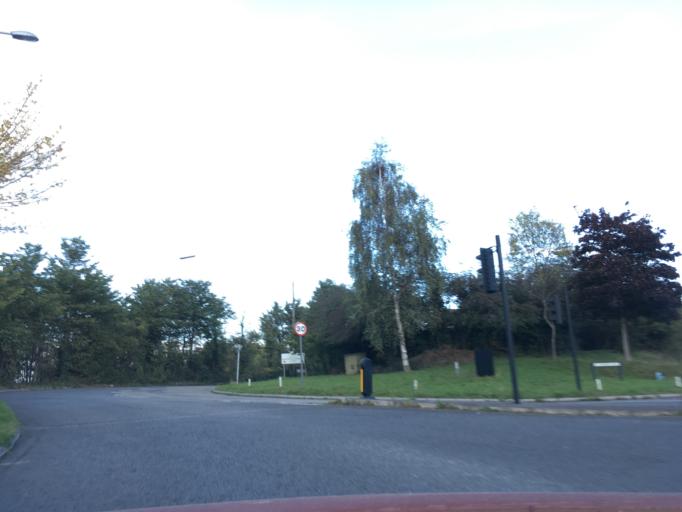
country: GB
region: England
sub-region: North Somerset
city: Easton-in-Gordano
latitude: 51.4745
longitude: -2.7053
